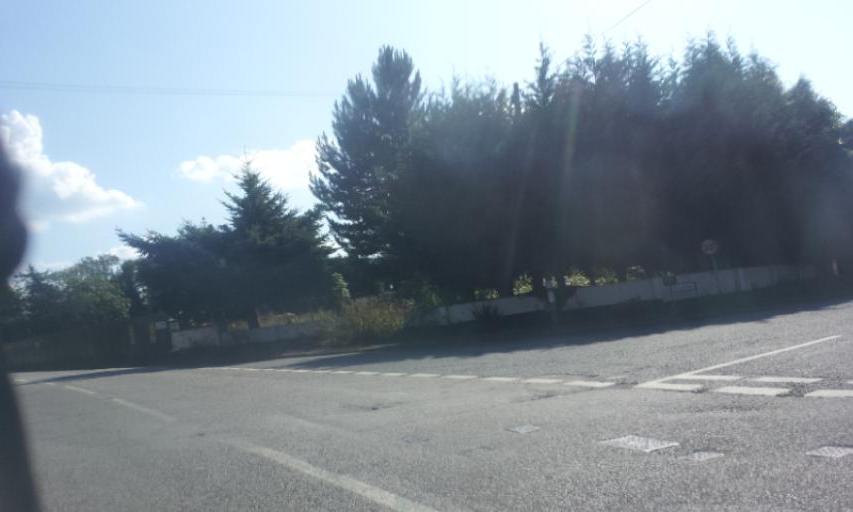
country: GB
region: England
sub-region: Kent
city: East Peckham
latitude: 51.2131
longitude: 0.3945
